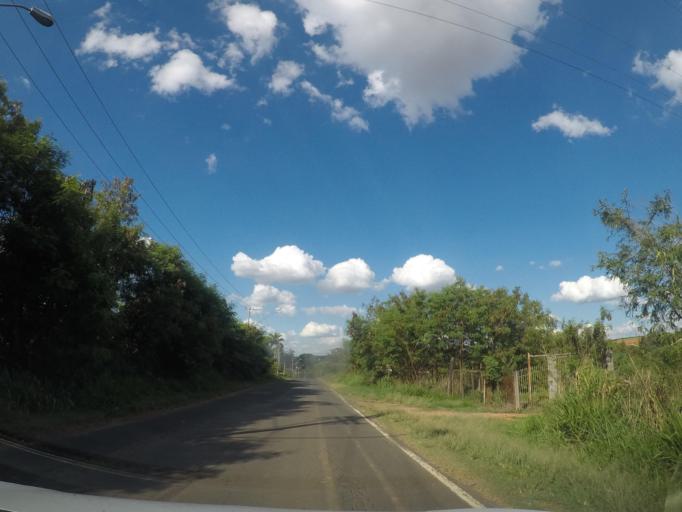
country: BR
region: Sao Paulo
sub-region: Sumare
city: Sumare
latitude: -22.8555
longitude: -47.2888
